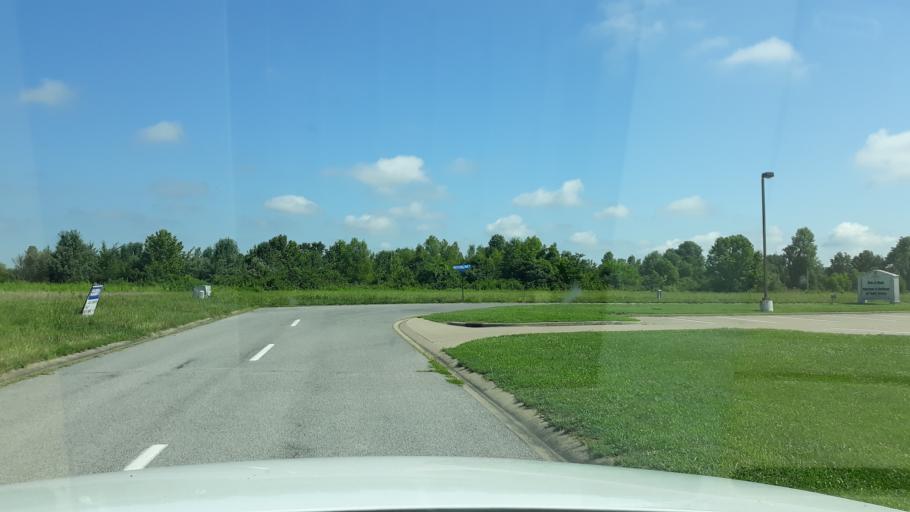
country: US
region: Illinois
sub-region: Williamson County
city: Energy
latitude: 37.7367
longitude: -88.9971
